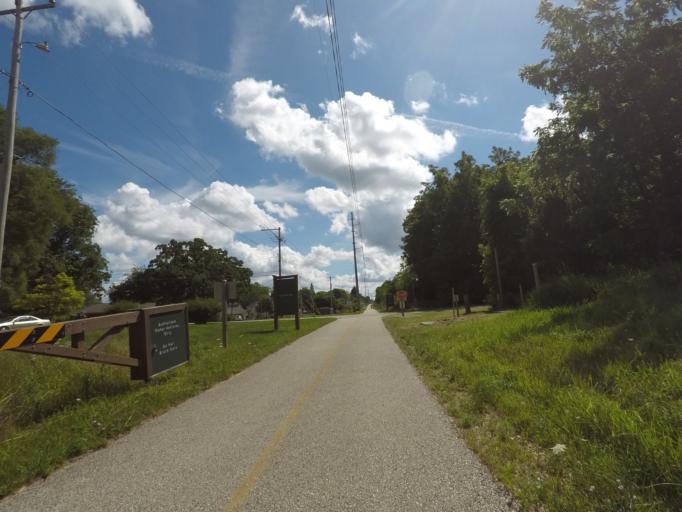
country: US
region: Wisconsin
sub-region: Waukesha County
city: Hartland
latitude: 43.0573
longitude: -88.3387
